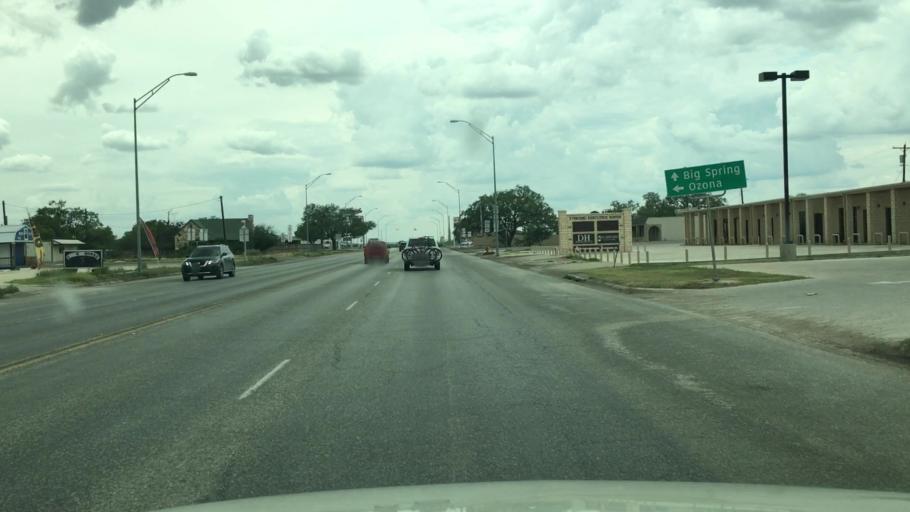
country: US
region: Texas
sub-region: Sterling County
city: Sterling City
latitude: 31.8366
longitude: -100.9907
